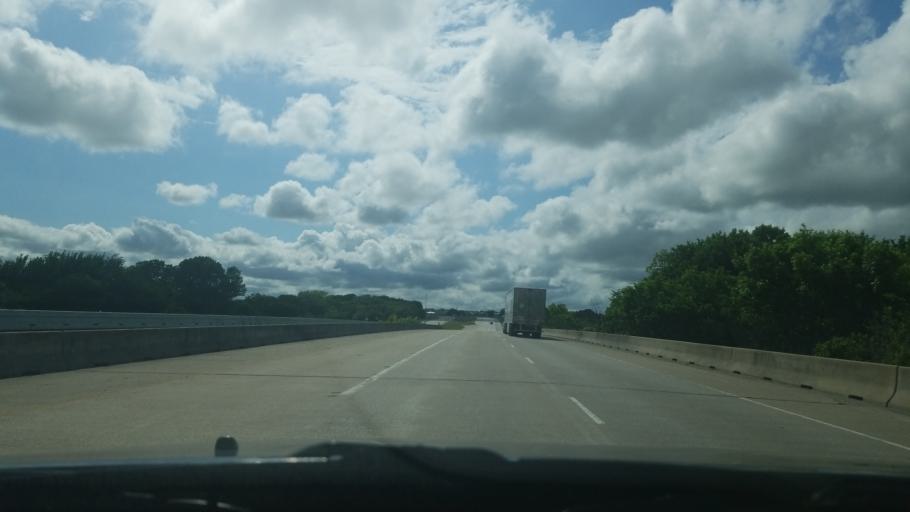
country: US
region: Texas
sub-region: Denton County
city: Ponder
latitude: 33.2493
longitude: -97.4032
